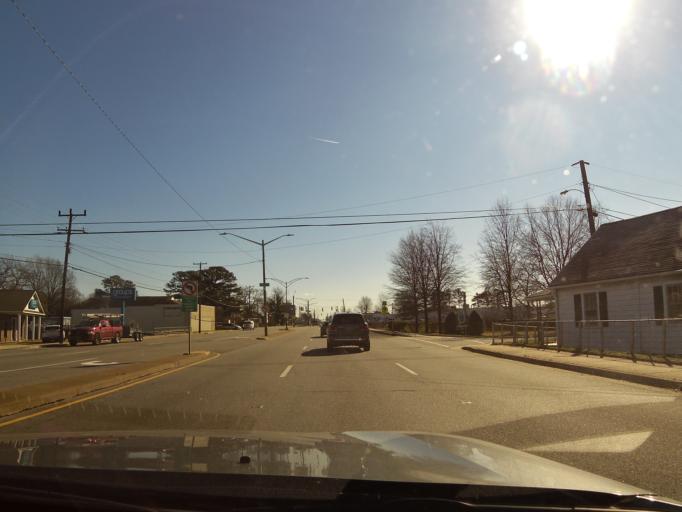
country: US
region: Virginia
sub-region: City of Newport News
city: Newport News
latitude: 37.0271
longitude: -76.4494
